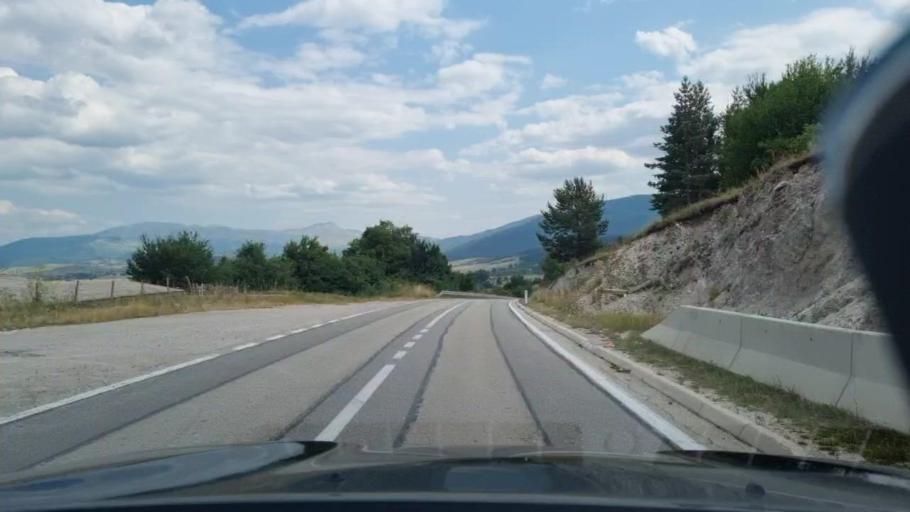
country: BA
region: Federation of Bosnia and Herzegovina
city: Bosansko Grahovo
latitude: 44.1805
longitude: 16.3689
